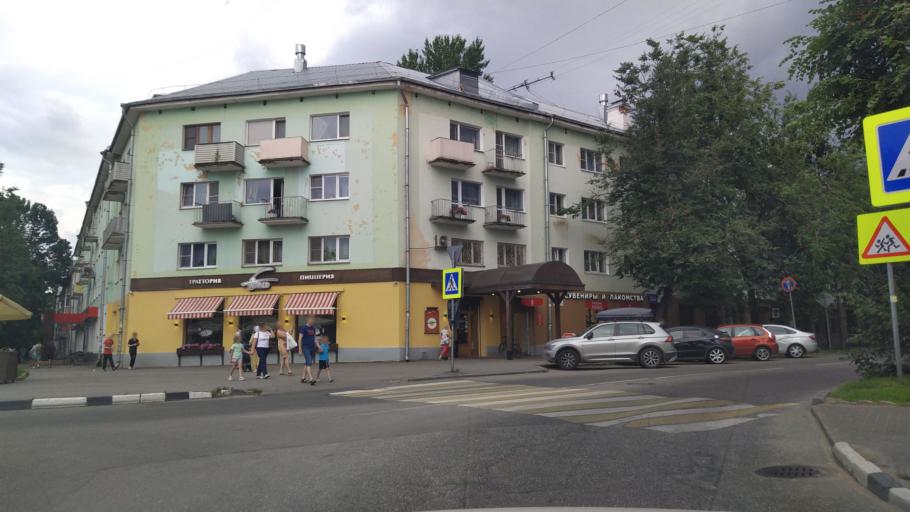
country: RU
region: Novgorod
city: Velikiy Novgorod
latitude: 58.5200
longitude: 31.2688
